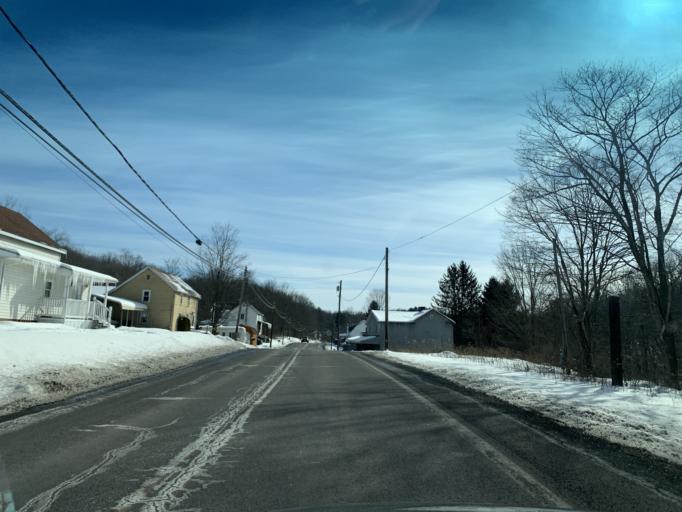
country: US
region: Maryland
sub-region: Allegany County
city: Lonaconing
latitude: 39.6041
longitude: -78.9447
